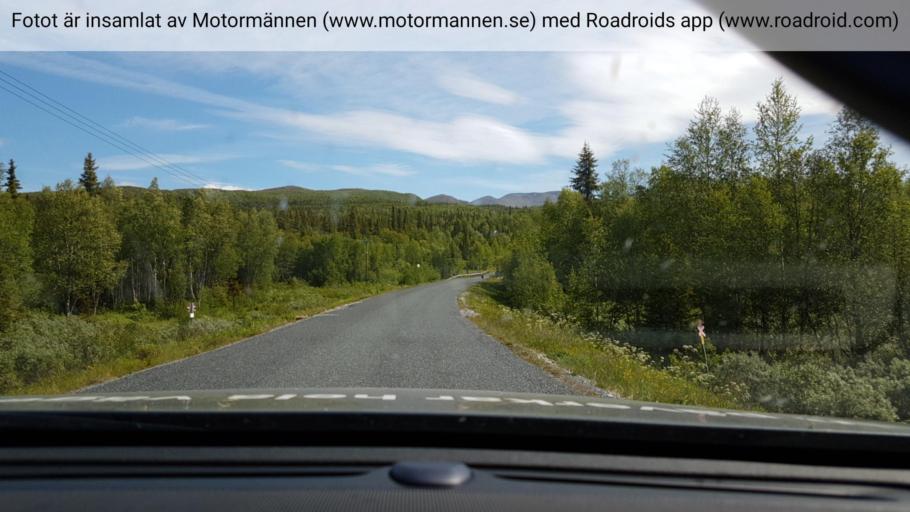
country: SE
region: Vaesterbotten
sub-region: Vilhelmina Kommun
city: Sjoberg
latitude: 65.2752
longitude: 15.3606
